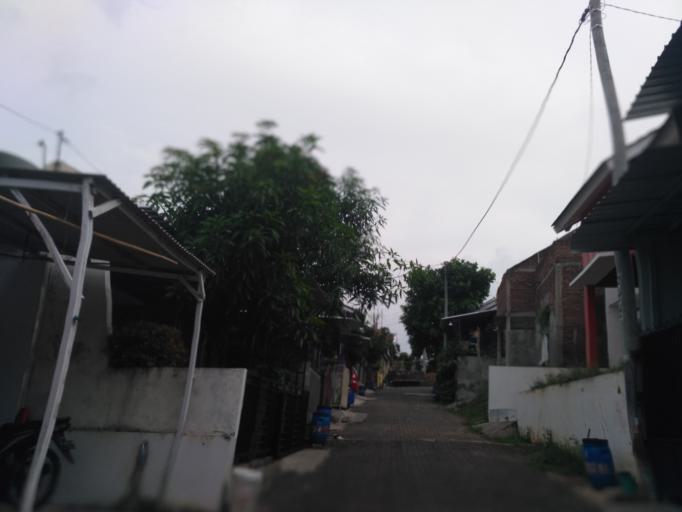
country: ID
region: Central Java
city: Ungaran
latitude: -7.0796
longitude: 110.4256
